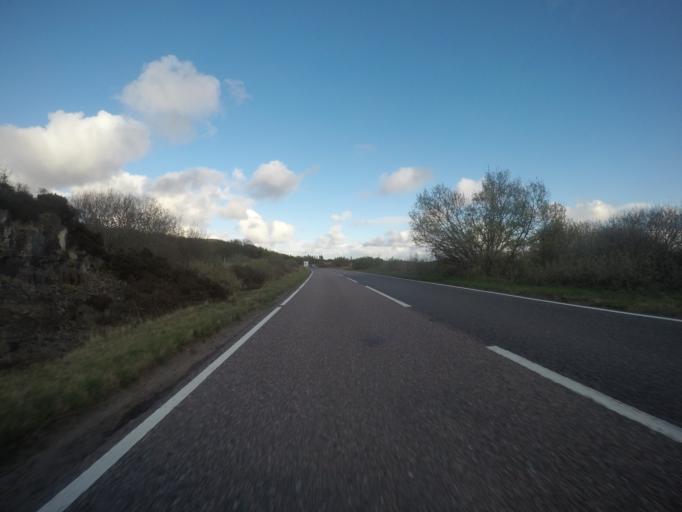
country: GB
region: Scotland
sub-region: Highland
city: Portree
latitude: 57.4587
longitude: -6.2766
